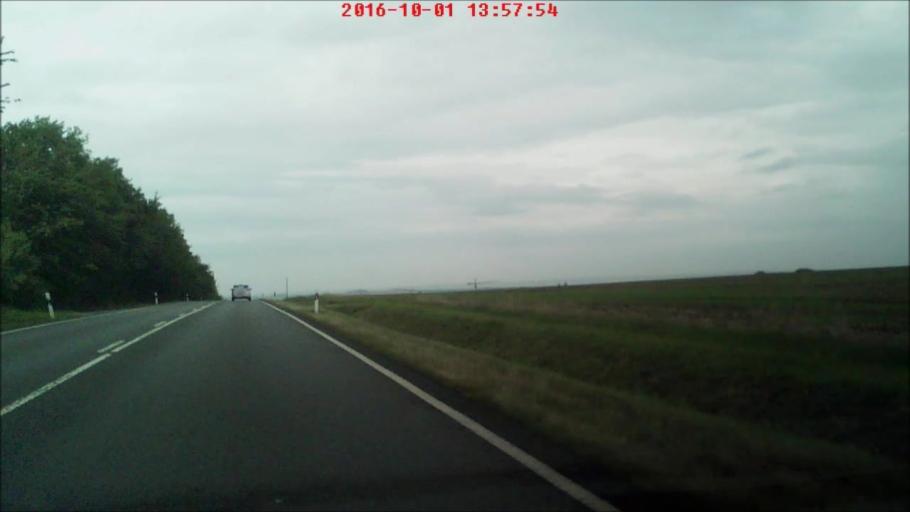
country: DE
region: Thuringia
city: Umpferstedt
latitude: 50.9653
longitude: 11.4092
